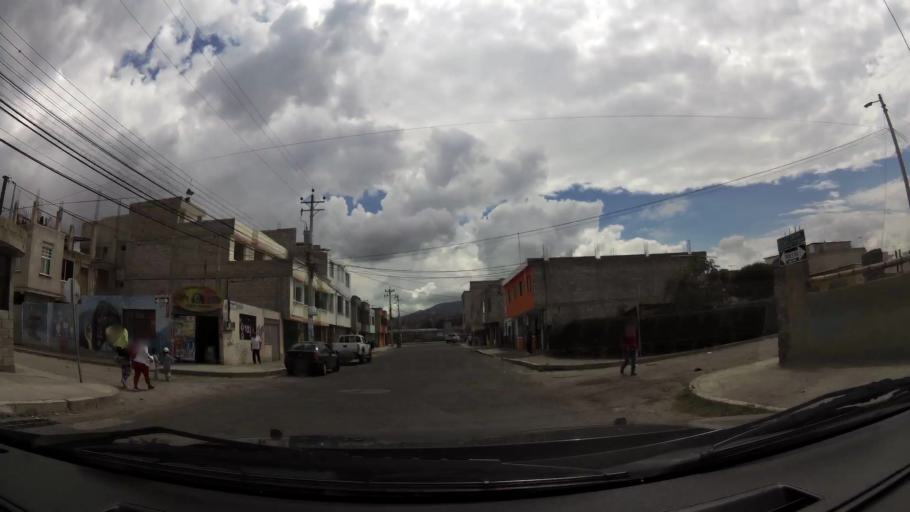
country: EC
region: Pichincha
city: Quito
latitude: -0.0796
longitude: -78.4146
